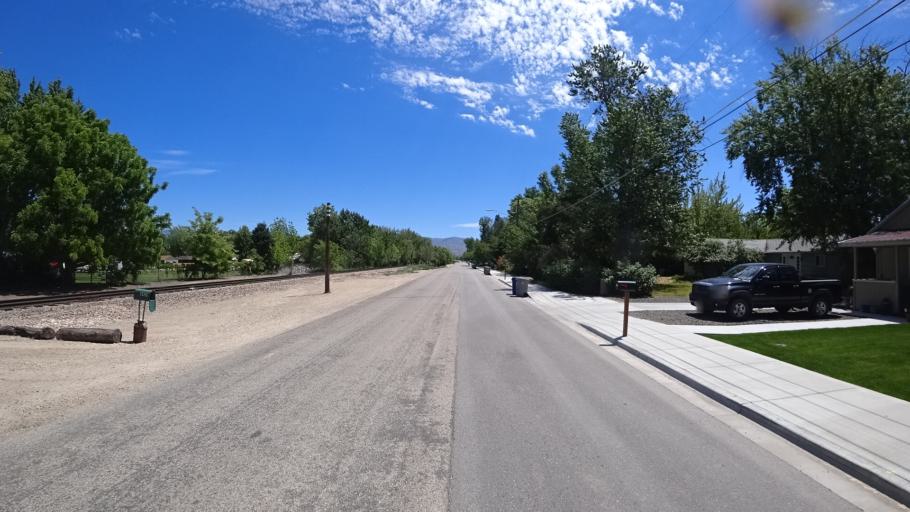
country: US
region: Idaho
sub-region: Ada County
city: Garden City
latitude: 43.6044
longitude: -116.2372
